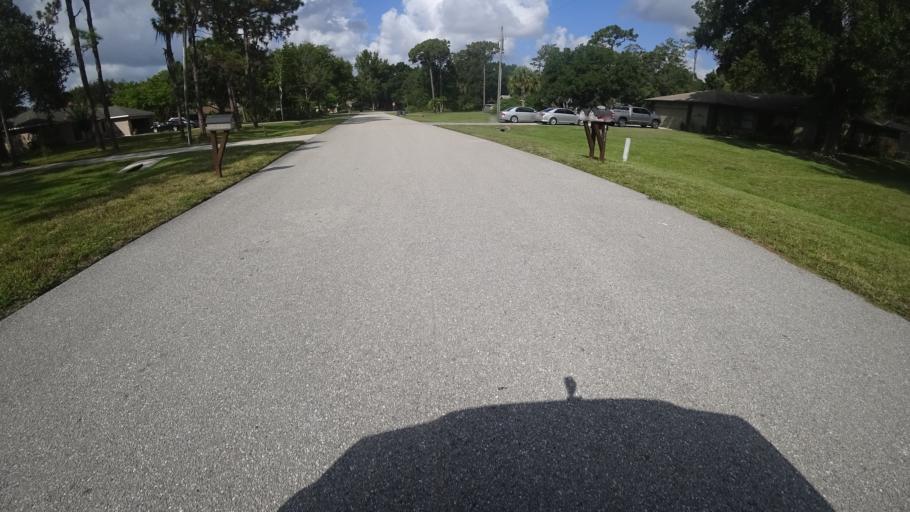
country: US
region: Florida
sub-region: Sarasota County
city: The Meadows
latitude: 27.4241
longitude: -82.4449
